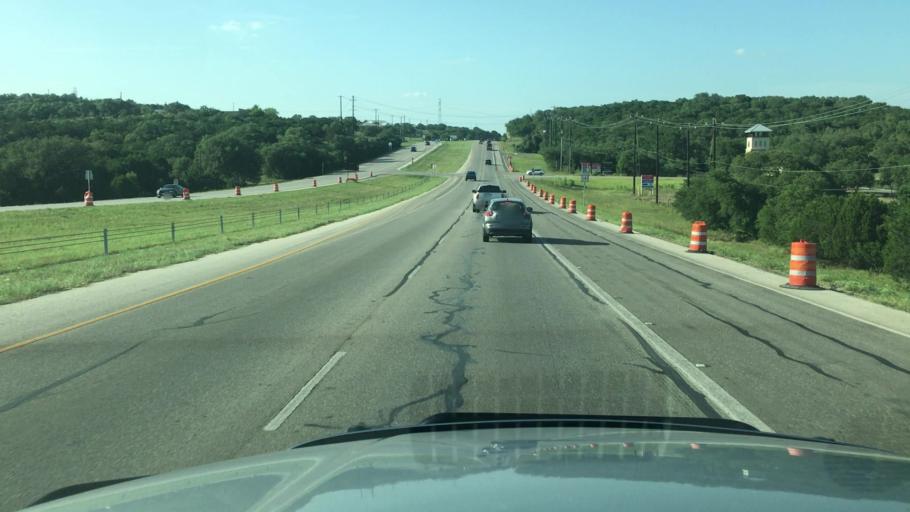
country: US
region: Texas
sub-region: Comal County
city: Bulverde
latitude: 29.7688
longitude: -98.4277
